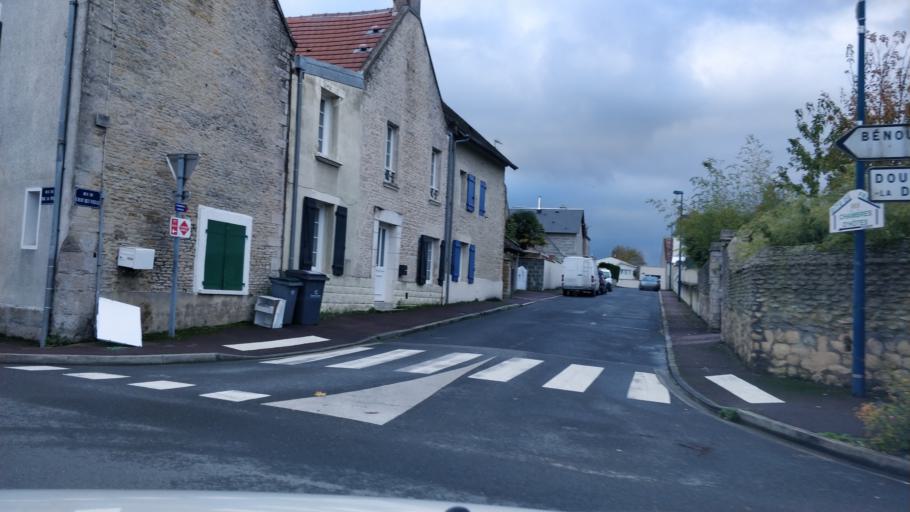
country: FR
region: Lower Normandy
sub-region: Departement du Calvados
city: Colleville-Montgomery
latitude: 49.2612
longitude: -0.2874
